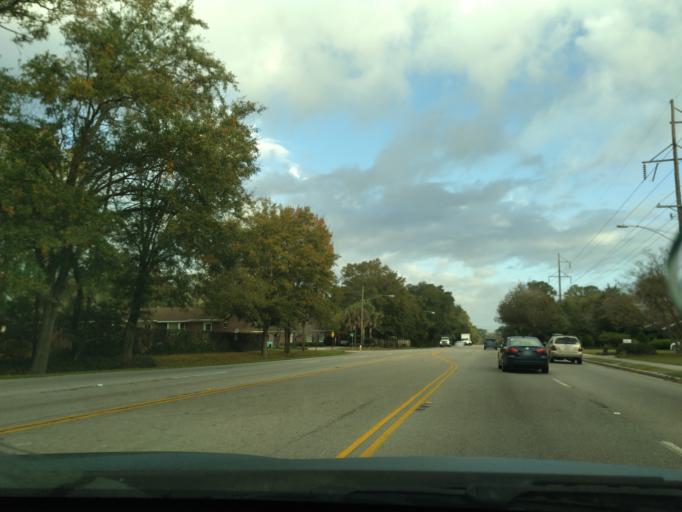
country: US
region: South Carolina
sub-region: Charleston County
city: North Charleston
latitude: 32.8001
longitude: -79.9964
